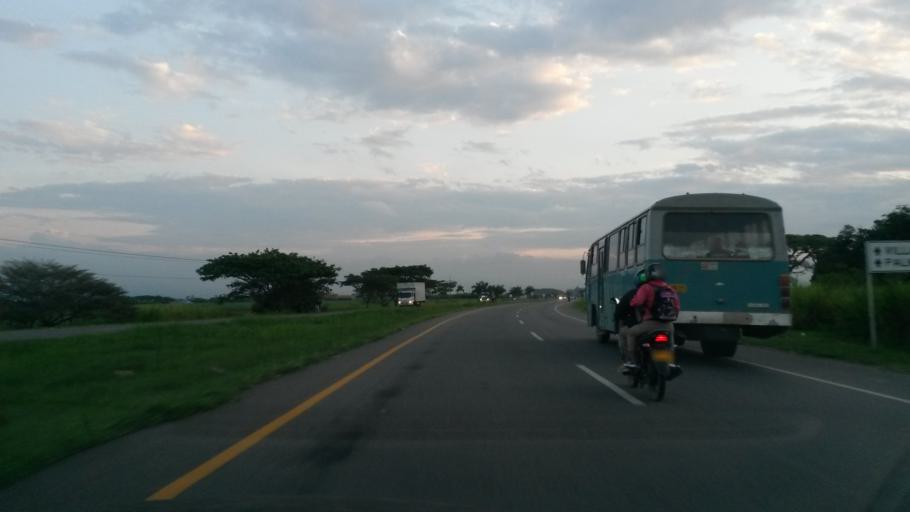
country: CO
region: Cauca
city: Santander de Quilichao
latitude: 3.0390
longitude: -76.4789
